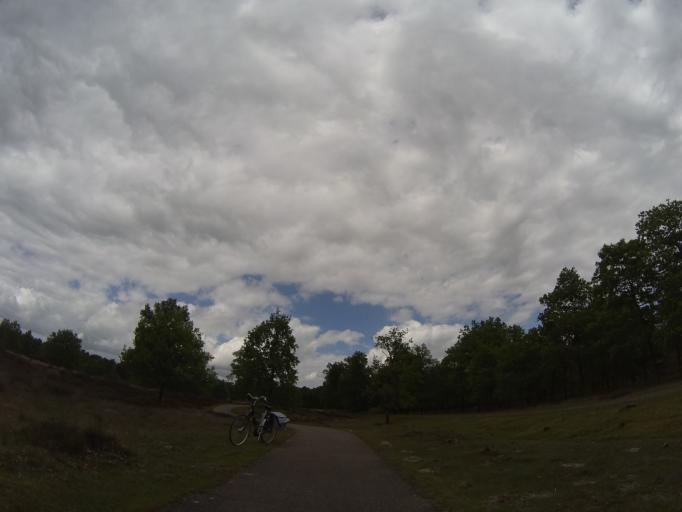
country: NL
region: Drenthe
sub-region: Gemeente Borger-Odoorn
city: Borger
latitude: 52.8669
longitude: 6.8123
